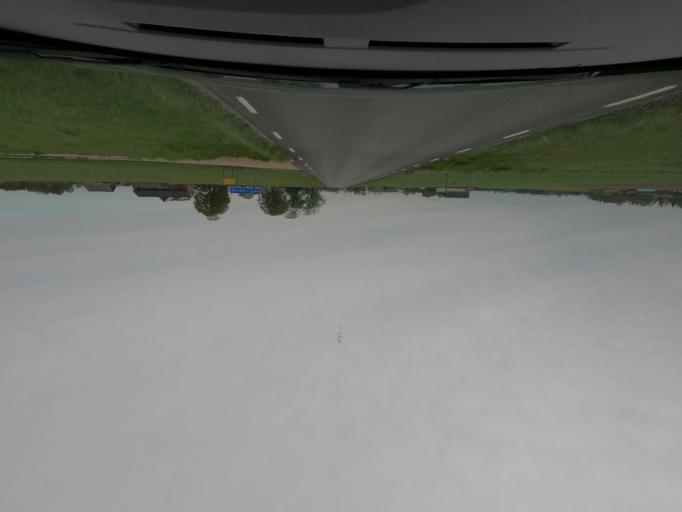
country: SE
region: Joenkoeping
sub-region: Varnamo Kommun
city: Bredaryd
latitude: 57.1390
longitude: 13.7124
